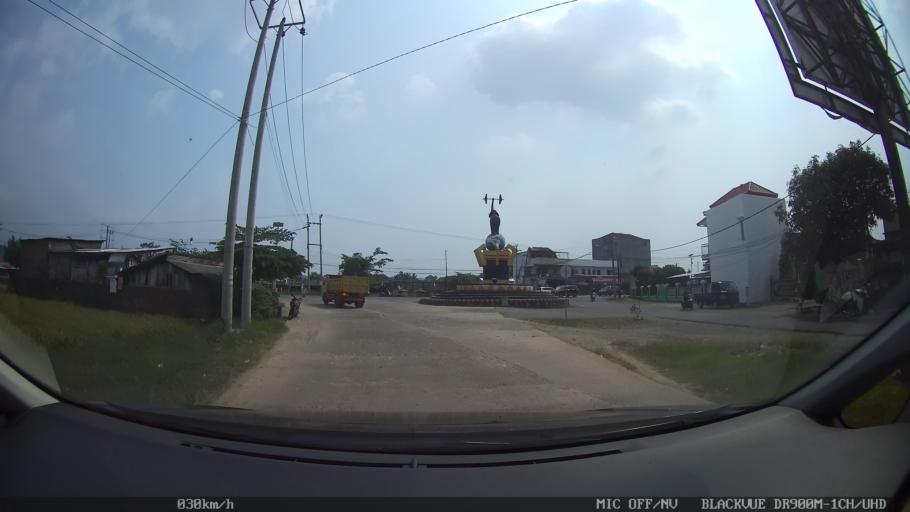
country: ID
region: Lampung
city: Pringsewu
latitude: -5.3633
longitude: 105.0046
